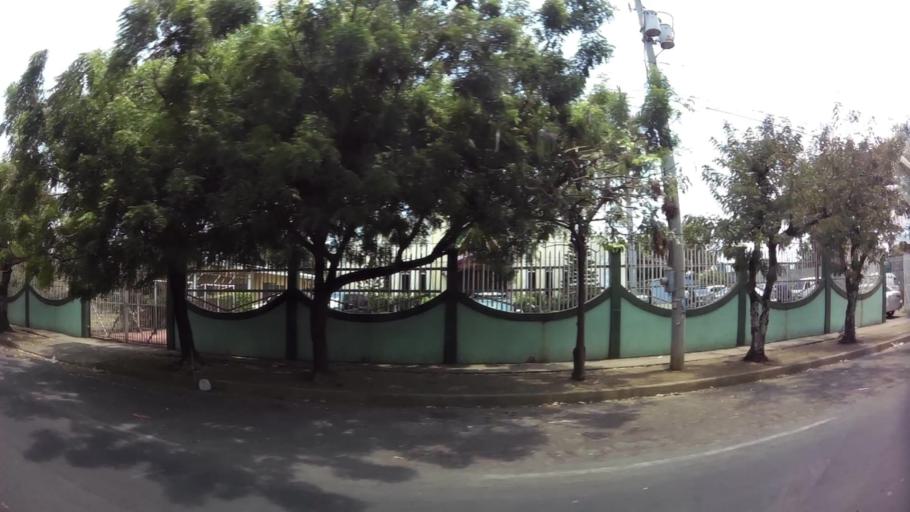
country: NI
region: Managua
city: Managua
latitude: 12.1450
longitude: -86.2938
